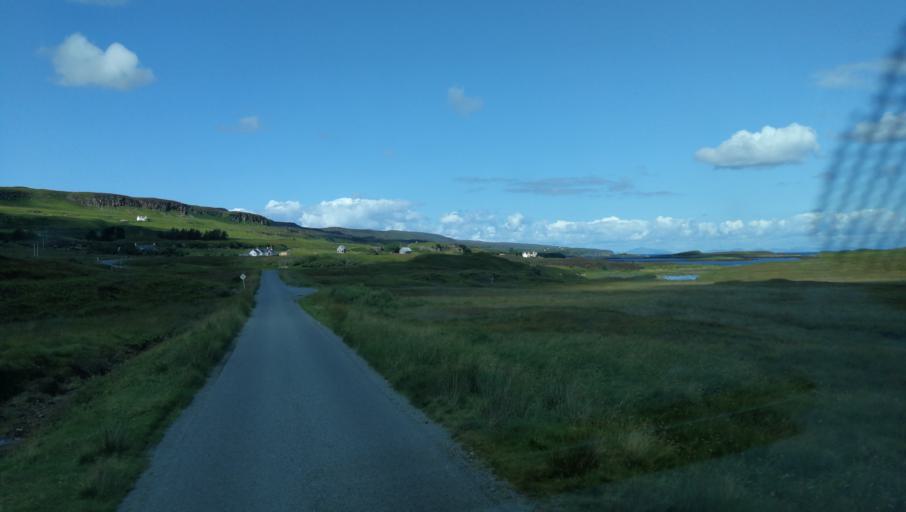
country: GB
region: Scotland
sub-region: Highland
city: Isle of Skye
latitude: 57.4301
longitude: -6.6180
